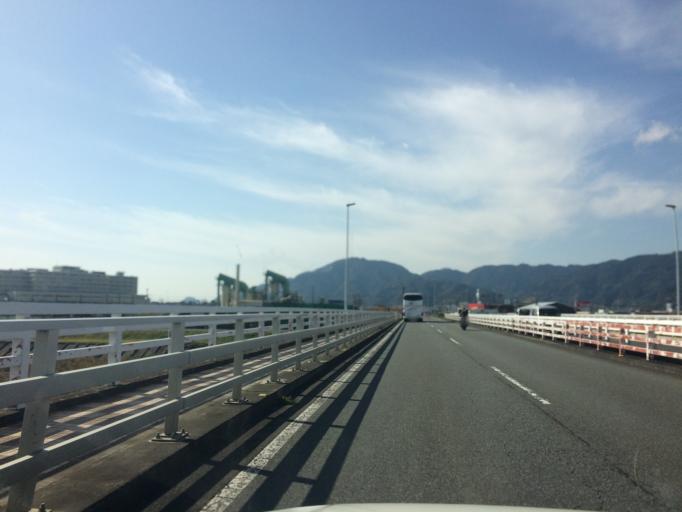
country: JP
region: Shizuoka
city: Shizuoka-shi
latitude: 34.9355
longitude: 138.3870
